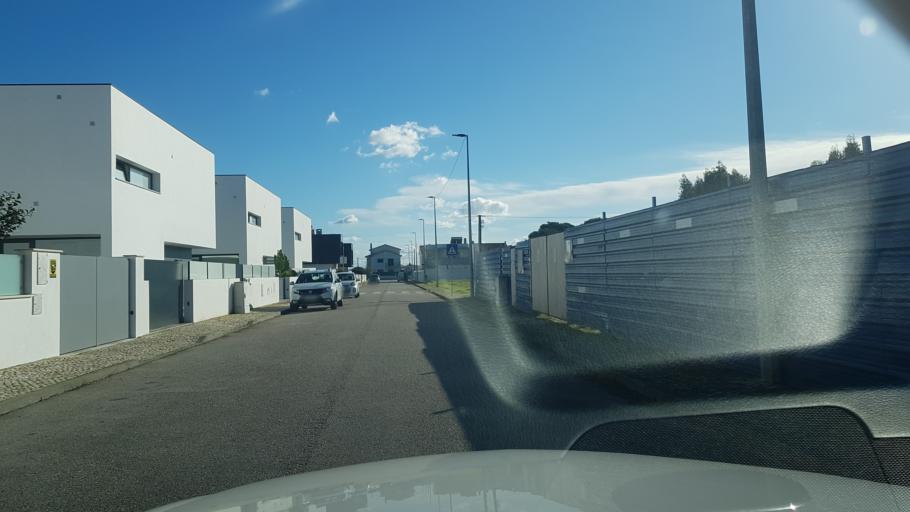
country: PT
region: Santarem
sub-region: Entroncamento
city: Entroncamento
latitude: 39.4792
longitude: -8.4783
